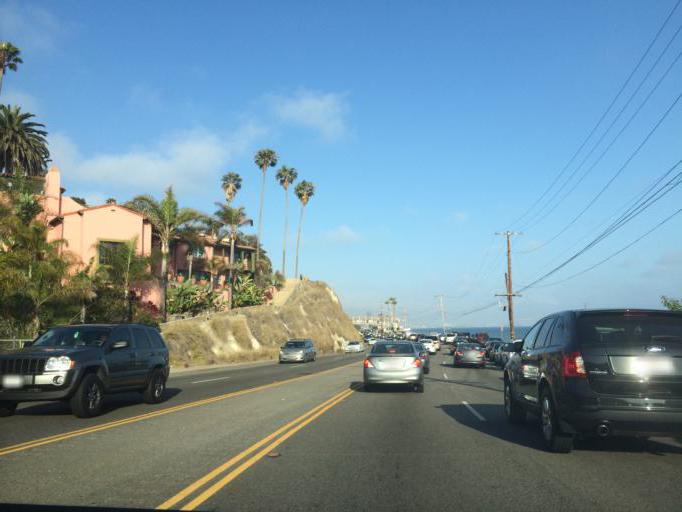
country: US
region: California
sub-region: Los Angeles County
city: Topanga
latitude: 34.0411
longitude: -118.5632
